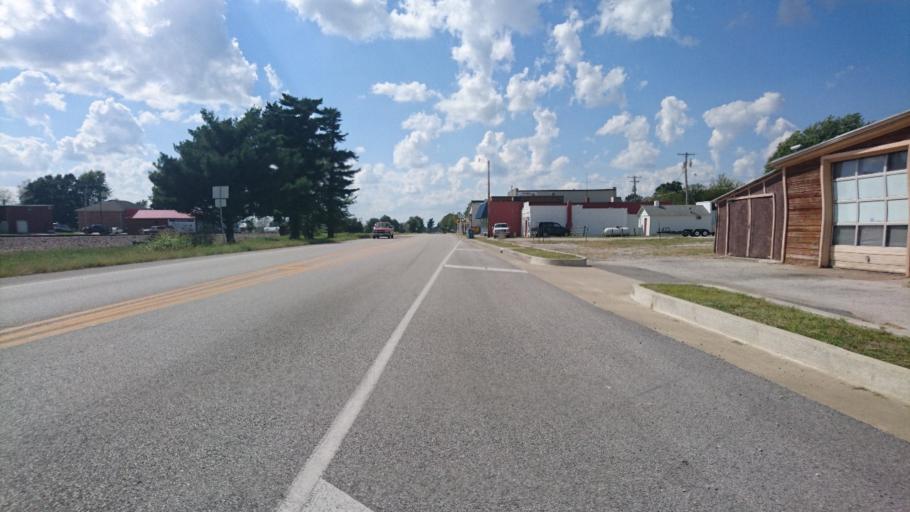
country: US
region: Missouri
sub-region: Greene County
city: Strafford
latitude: 37.2687
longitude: -93.1156
